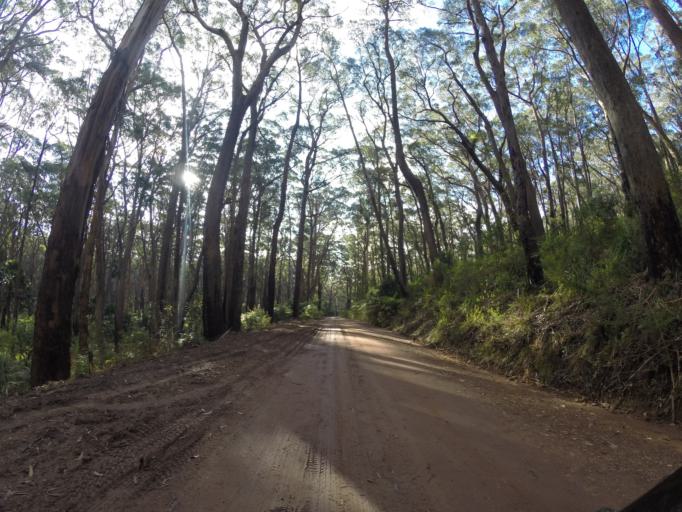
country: AU
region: New South Wales
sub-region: Wollongong
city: Cordeaux Heights
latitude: -34.4182
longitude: 150.7840
